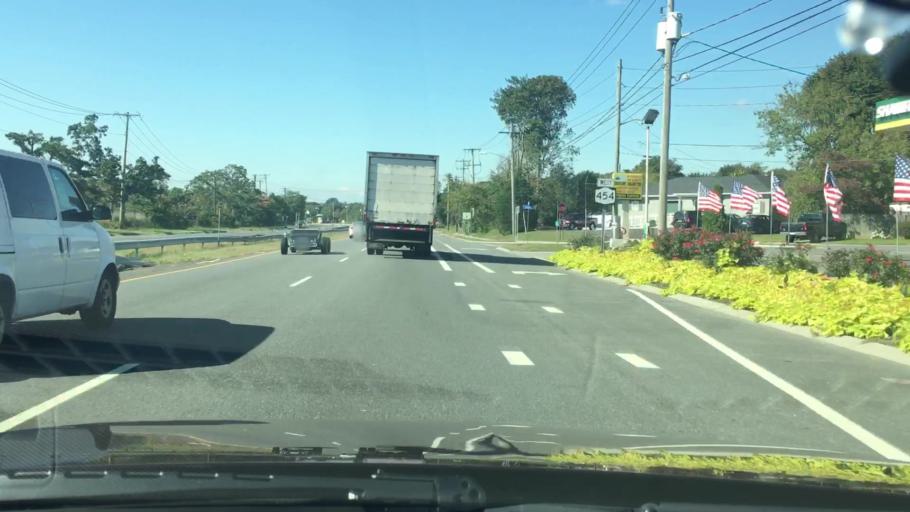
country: US
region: New York
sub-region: Suffolk County
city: Holbrook
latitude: 40.7794
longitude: -73.0762
